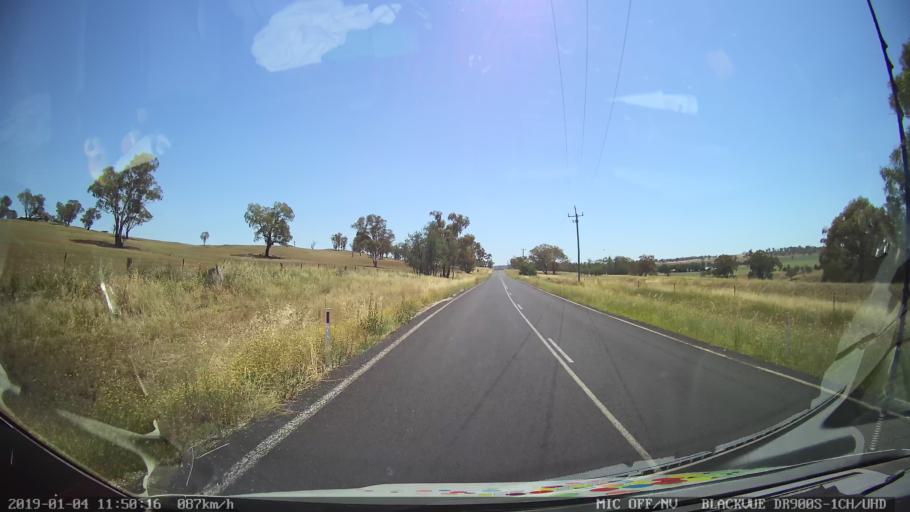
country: AU
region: New South Wales
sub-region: Cabonne
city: Molong
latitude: -32.9083
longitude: 148.7558
